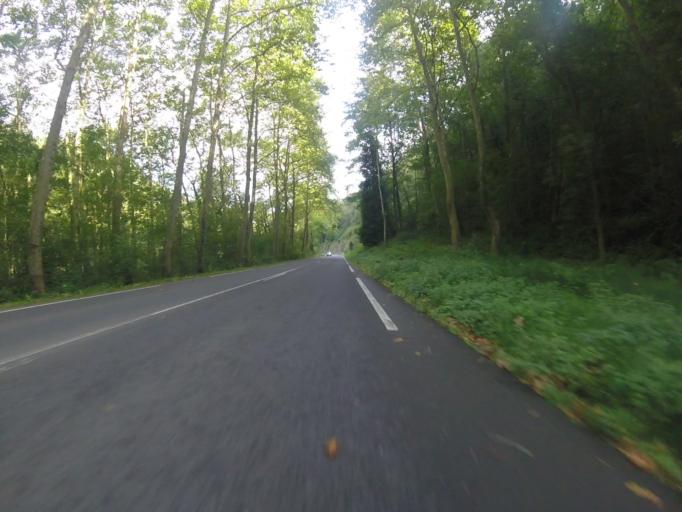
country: ES
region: Basque Country
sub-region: Provincia de Guipuzcoa
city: Orendain
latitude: 43.0772
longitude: -2.0879
